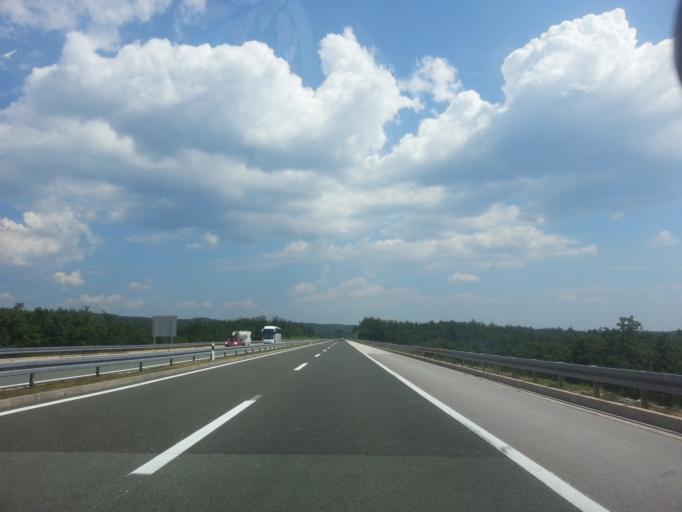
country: HR
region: Primorsko-Goranska
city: Matulji
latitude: 45.4326
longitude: 14.2849
